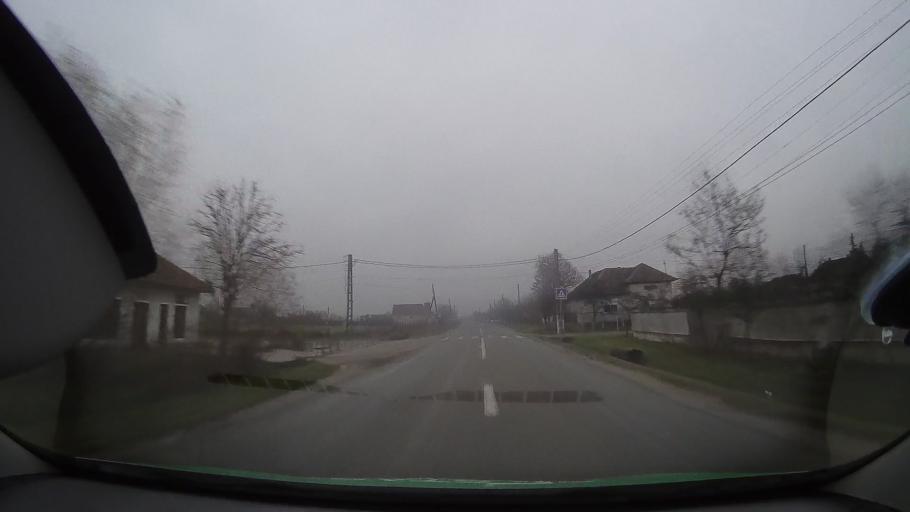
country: RO
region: Bihor
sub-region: Comuna Tulca
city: Tulca
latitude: 46.7938
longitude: 21.7451
